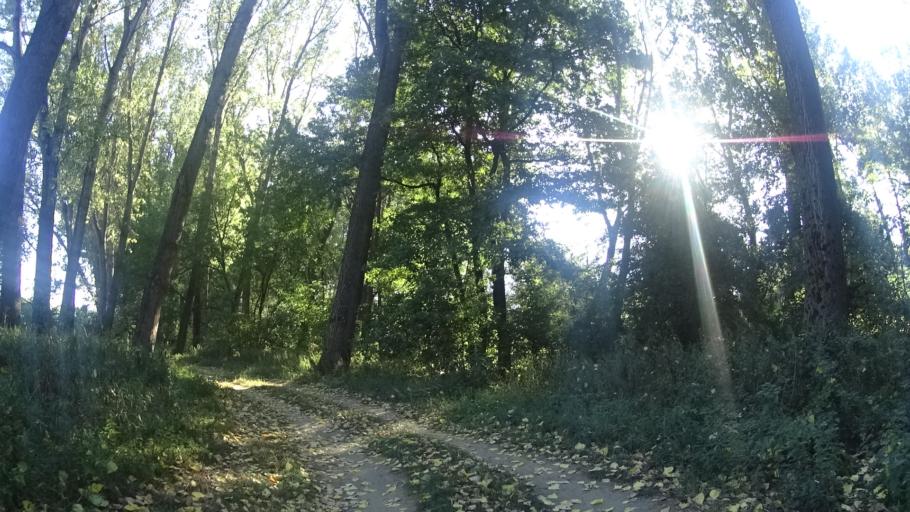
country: AT
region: Lower Austria
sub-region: Politischer Bezirk Mistelbach
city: Rabensburg
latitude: 48.6170
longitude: 16.9414
